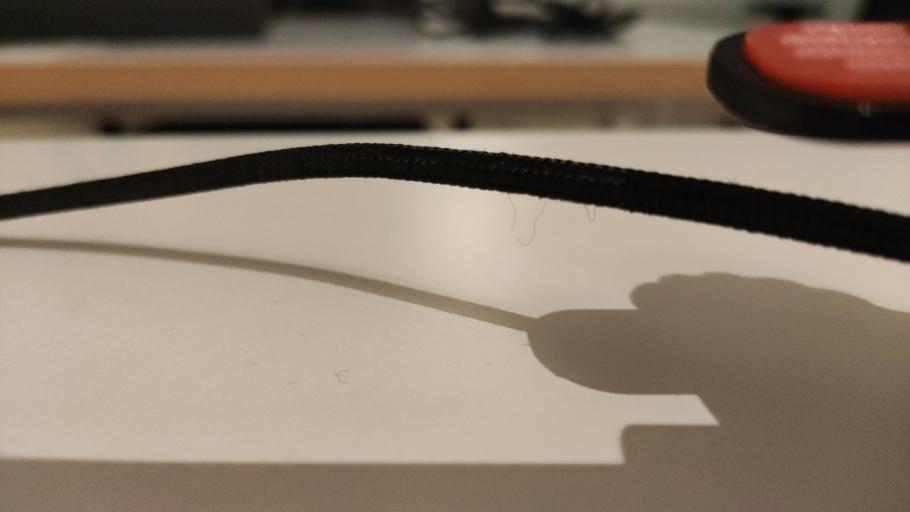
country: RU
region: Moskovskaya
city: Kurovskoye
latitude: 55.5753
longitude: 38.8875
